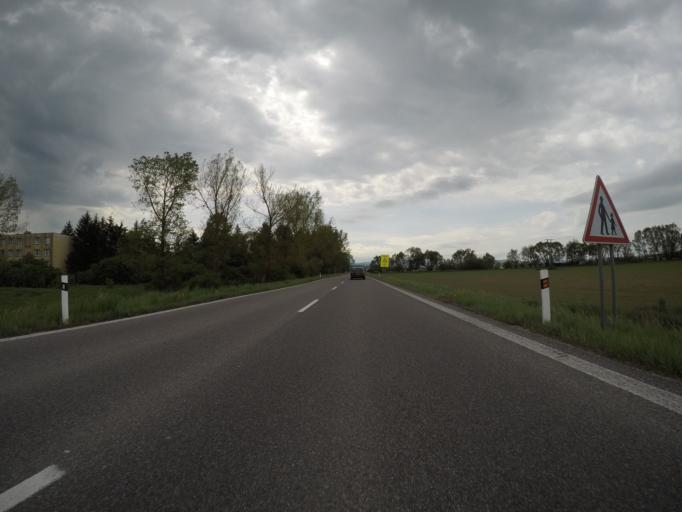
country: SK
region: Banskobystricky
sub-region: Okres Banska Bystrica
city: Banska Bystrica
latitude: 48.6609
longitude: 19.1422
